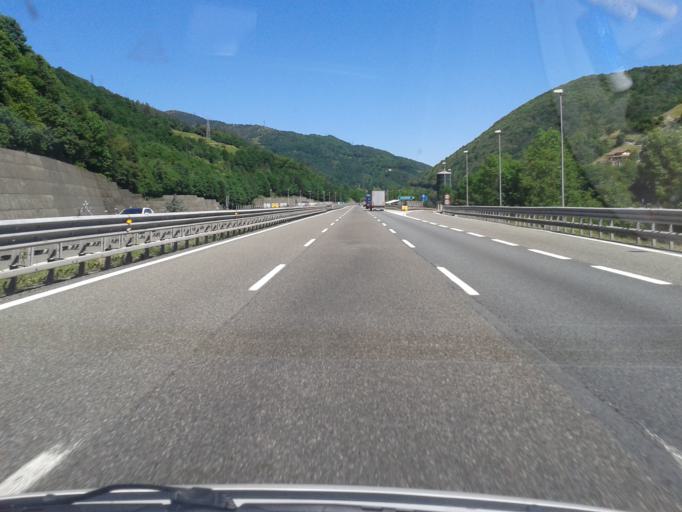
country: IT
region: Liguria
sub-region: Provincia di Genova
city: Masone
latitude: 44.5023
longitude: 8.7071
